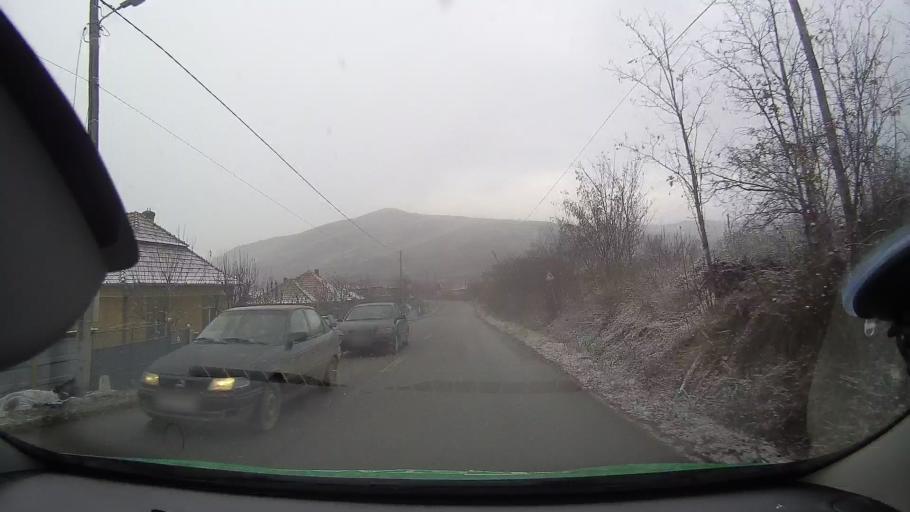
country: RO
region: Alba
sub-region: Comuna Noslac
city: Noslac
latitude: 46.3647
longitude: 23.9317
